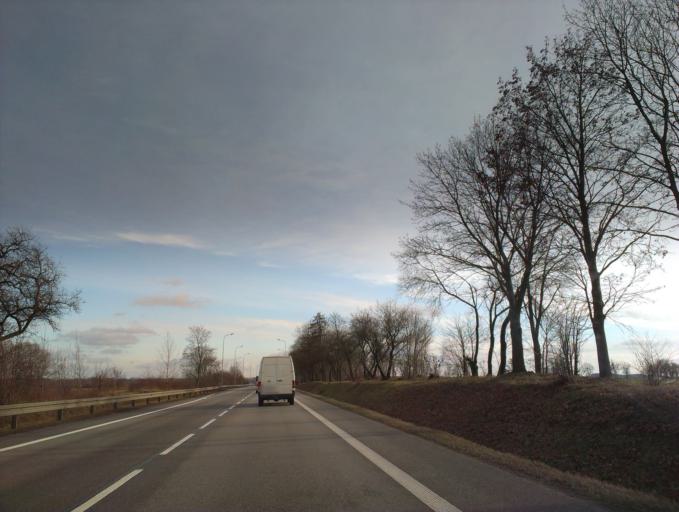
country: PL
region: Kujawsko-Pomorskie
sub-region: Powiat lipnowski
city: Kikol
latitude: 52.9284
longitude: 19.0781
